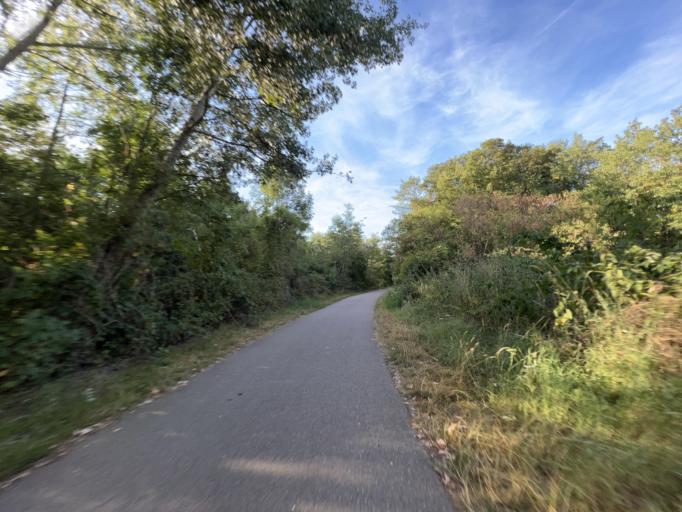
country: DE
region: North Rhine-Westphalia
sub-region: Regierungsbezirk Koln
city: Dueren
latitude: 50.8157
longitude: 6.4570
